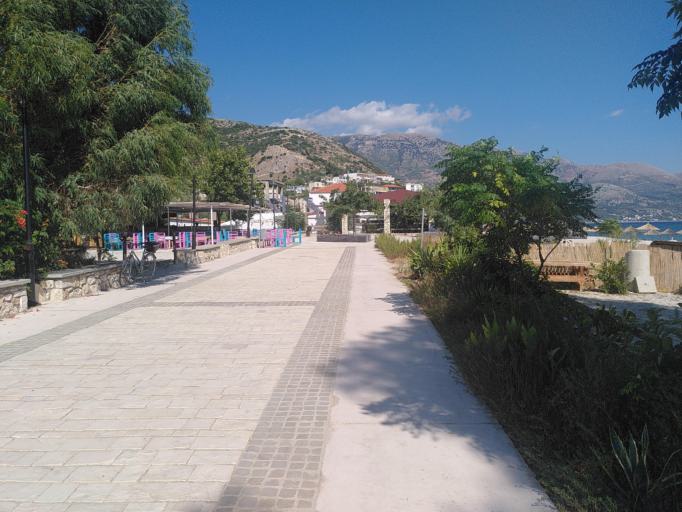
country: AL
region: Vlore
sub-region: Rrethi i Vlores
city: Himare
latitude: 40.0532
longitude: 19.8231
